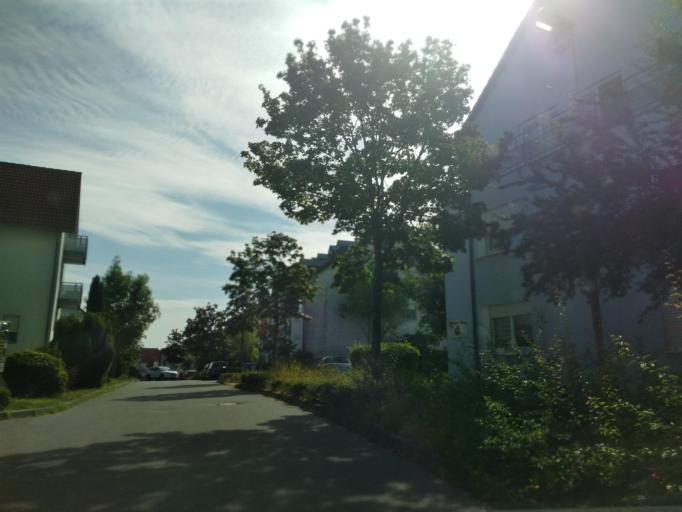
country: DE
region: Baden-Wuerttemberg
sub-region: Karlsruhe Region
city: Buchen
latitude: 49.5181
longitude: 9.3037
